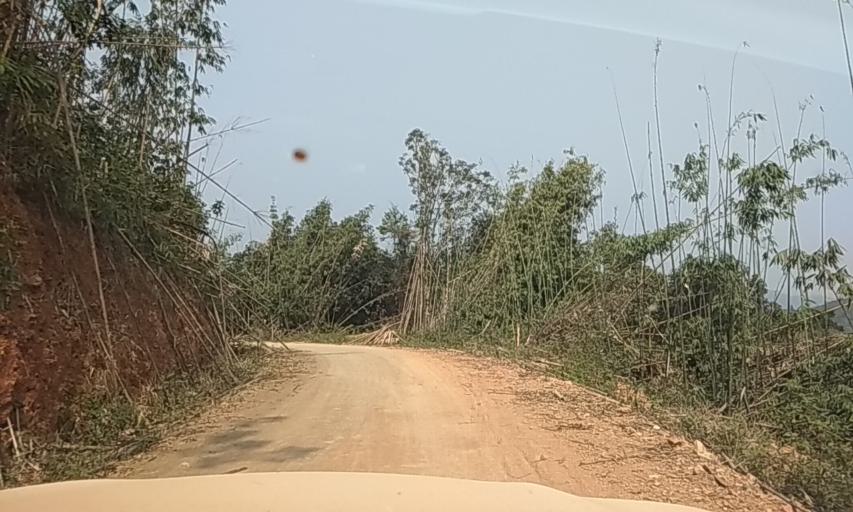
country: LA
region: Phongsali
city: Phongsali
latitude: 21.4693
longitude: 102.4238
